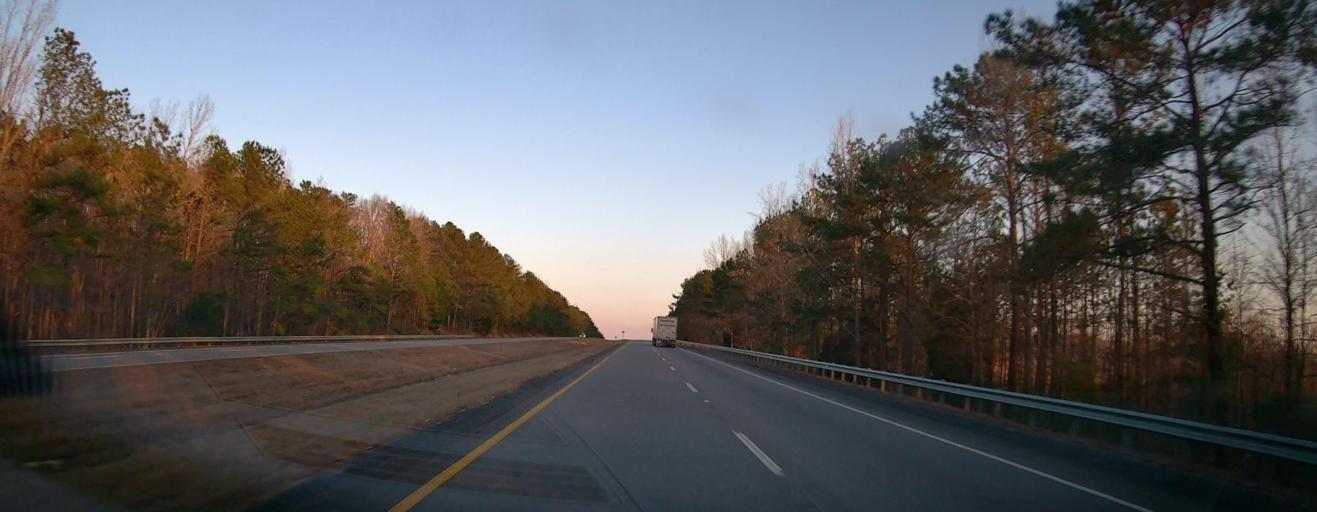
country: US
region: Alabama
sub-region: Coosa County
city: Goodwater
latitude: 33.0455
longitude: -86.1365
